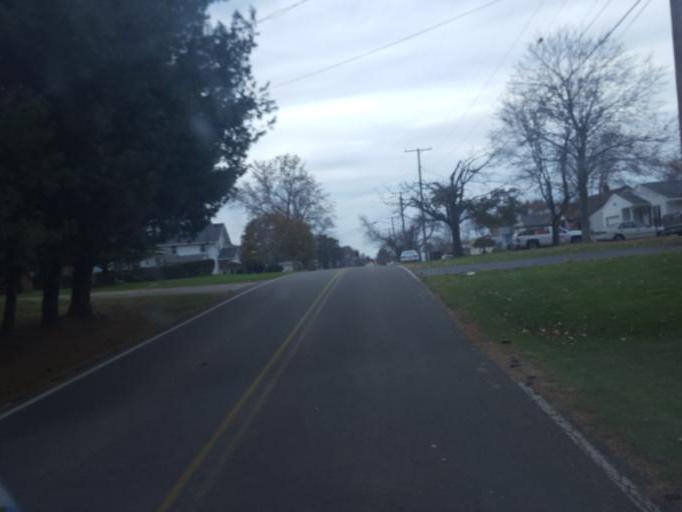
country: US
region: Ohio
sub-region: Richland County
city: Ontario
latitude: 40.7562
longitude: -82.5637
